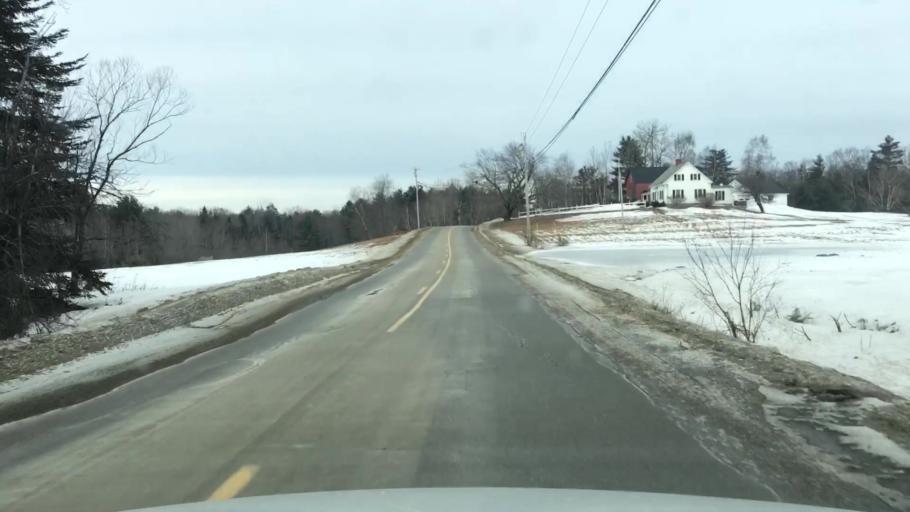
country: US
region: Maine
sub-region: Kennebec County
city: Chelsea
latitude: 44.2651
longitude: -69.6492
